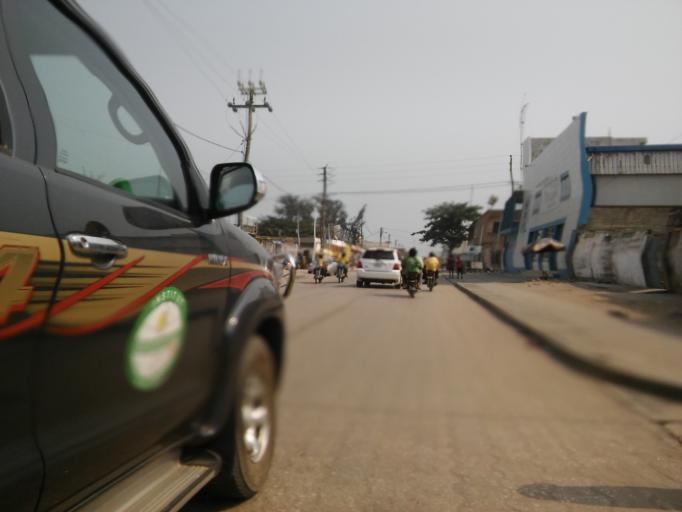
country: BJ
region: Littoral
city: Cotonou
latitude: 6.3771
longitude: 2.4119
